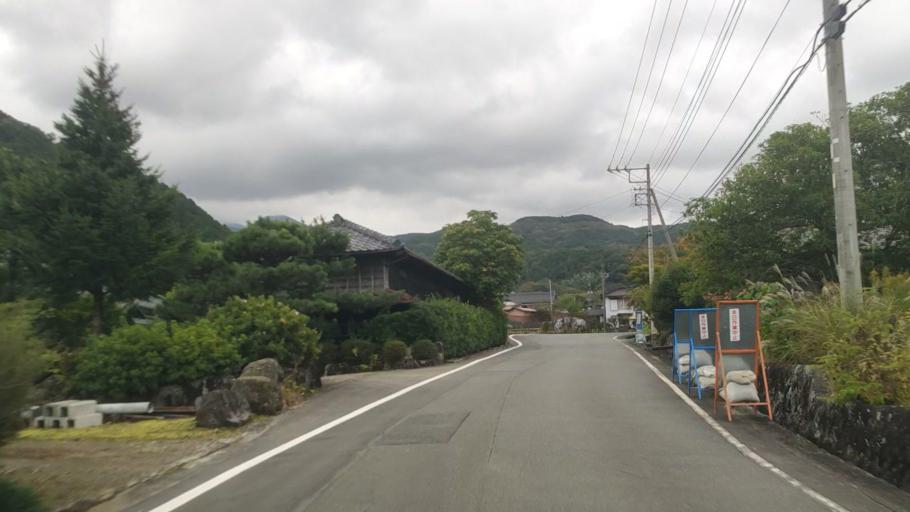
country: JP
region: Shizuoka
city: Ito
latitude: 34.9179
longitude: 138.9931
